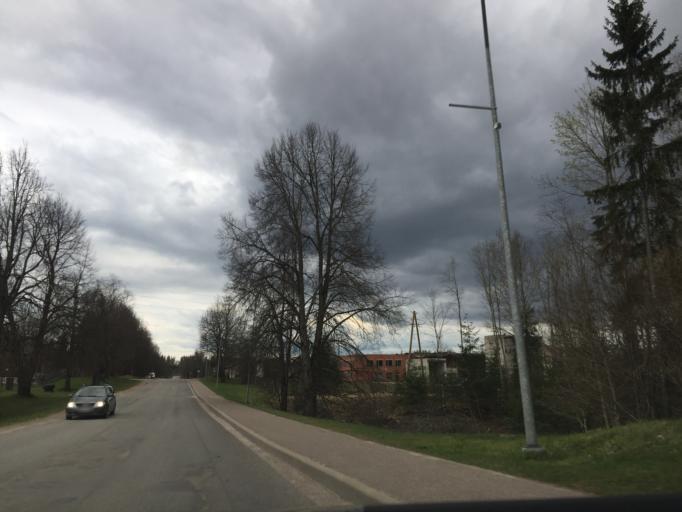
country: LV
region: Aluksnes Rajons
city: Aluksne
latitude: 57.4083
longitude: 27.0444
